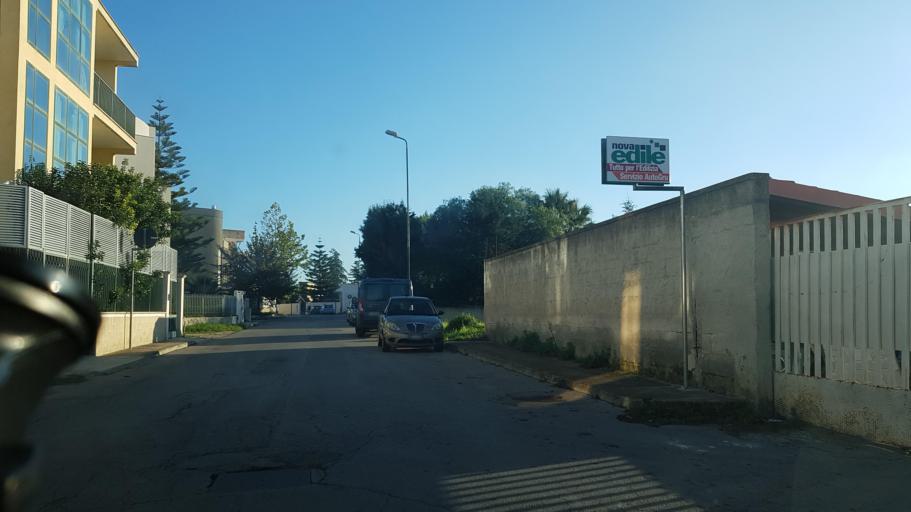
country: IT
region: Apulia
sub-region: Provincia di Brindisi
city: Latiano
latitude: 40.5497
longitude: 17.7241
